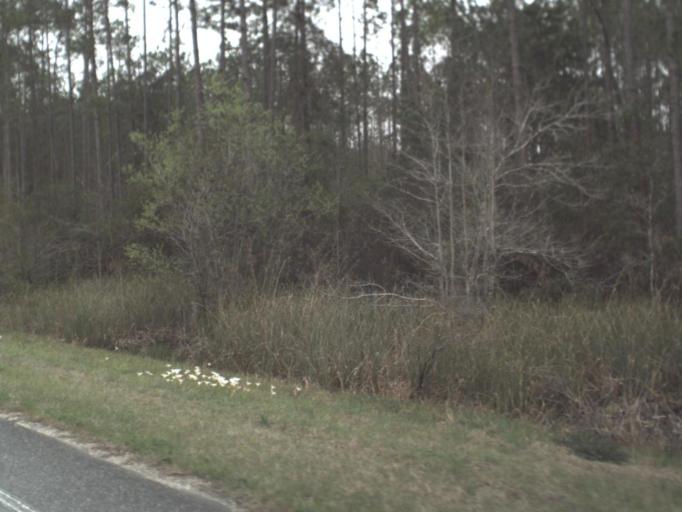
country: US
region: Florida
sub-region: Leon County
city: Woodville
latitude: 30.1925
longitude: -84.1037
